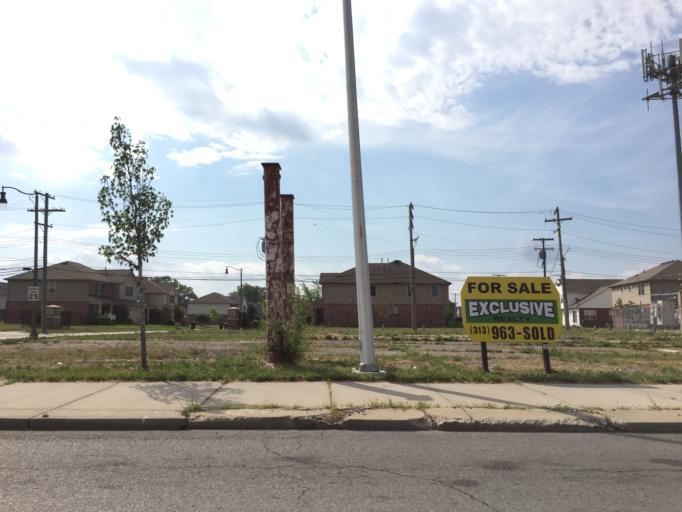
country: US
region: Michigan
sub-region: Wayne County
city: Grosse Pointe Park
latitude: 42.3637
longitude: -82.9773
